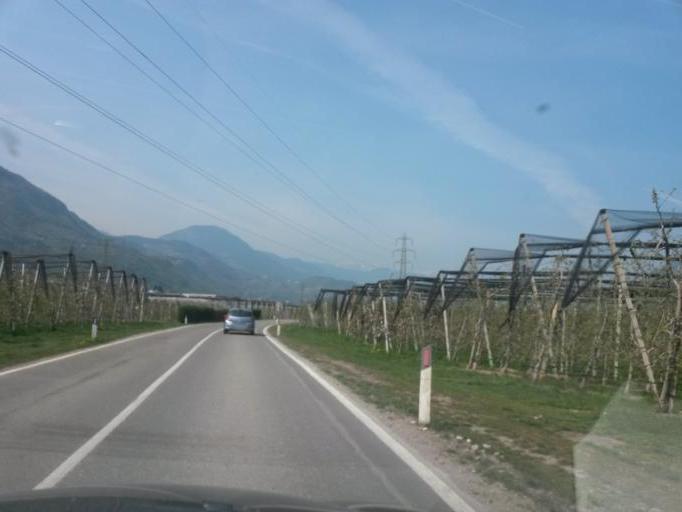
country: IT
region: Trentino-Alto Adige
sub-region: Bolzano
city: Terlano
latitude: 46.5171
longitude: 11.2467
